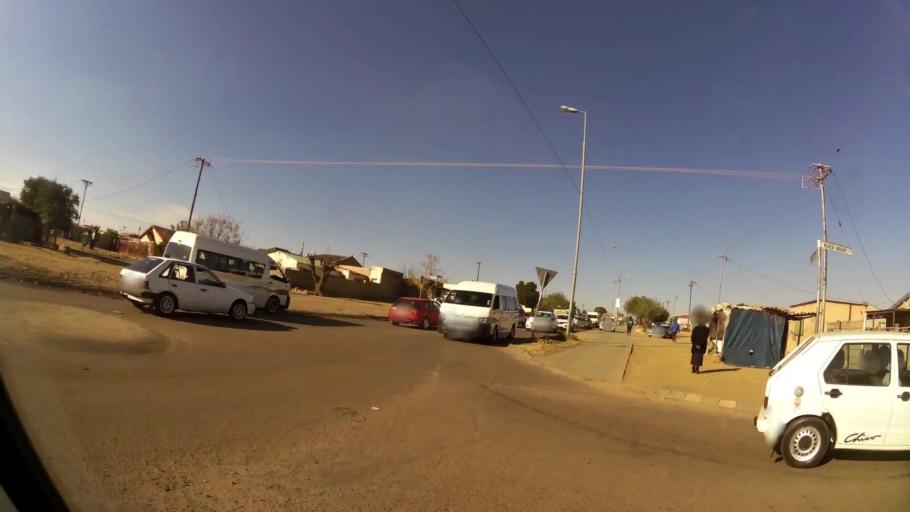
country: ZA
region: Gauteng
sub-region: City of Tshwane Metropolitan Municipality
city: Cullinan
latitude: -25.7211
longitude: 28.3823
